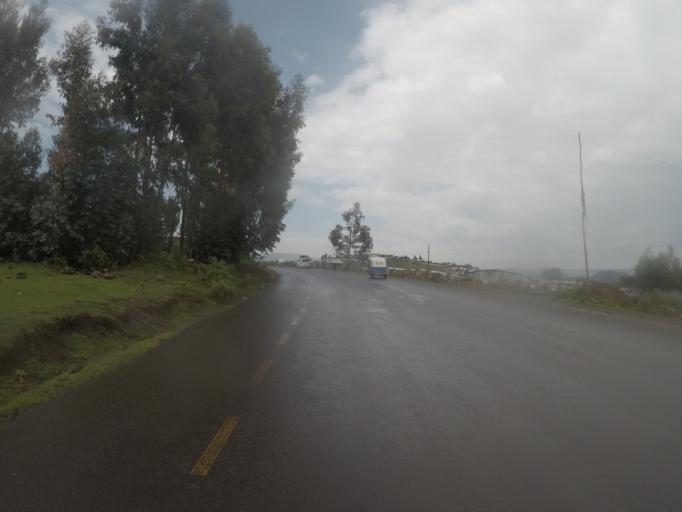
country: ET
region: Amhara
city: Debark'
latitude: 13.1376
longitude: 37.8939
